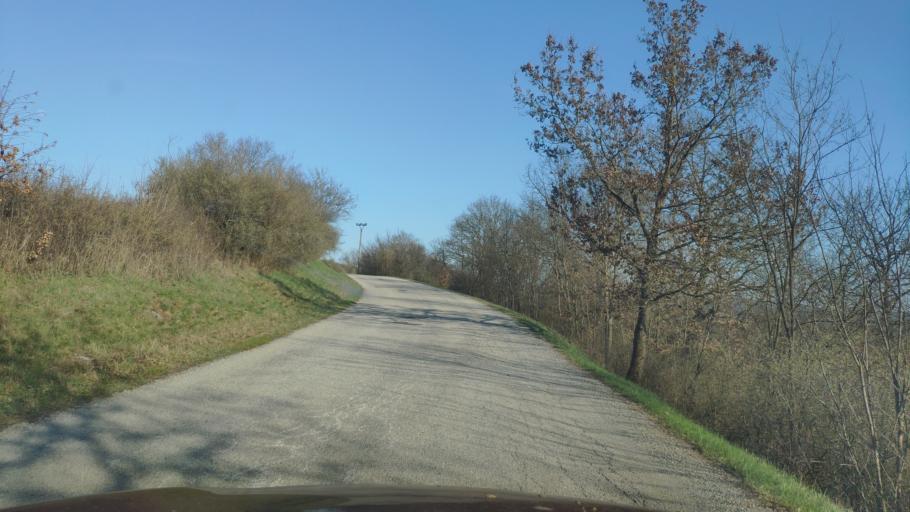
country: SK
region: Banskobystricky
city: Revuca
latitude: 48.4995
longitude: 20.2556
